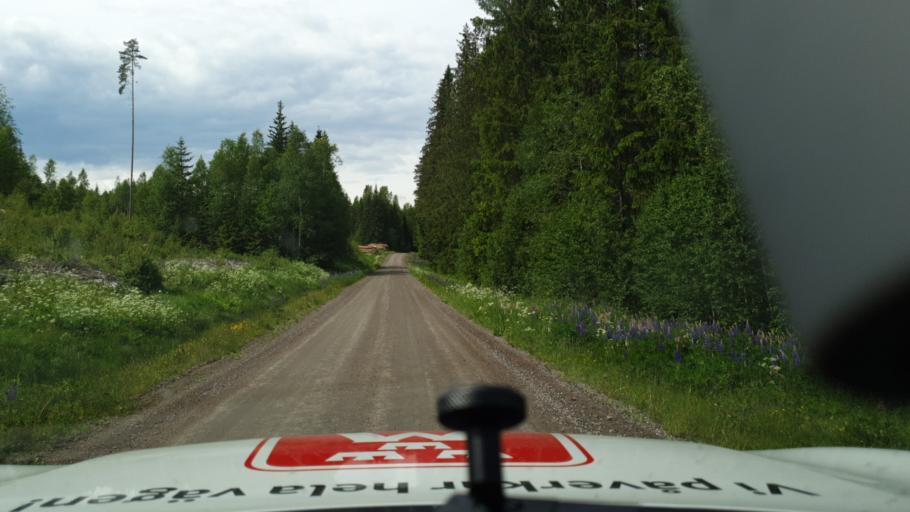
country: SE
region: Vaermland
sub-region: Torsby Kommun
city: Torsby
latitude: 59.9786
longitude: 12.8450
